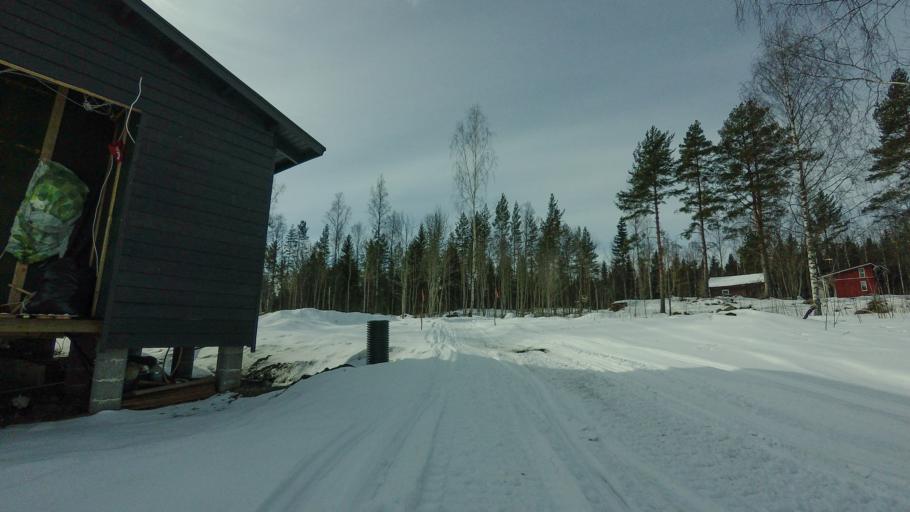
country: FI
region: Southern Savonia
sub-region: Savonlinna
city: Rantasalmi
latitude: 62.1206
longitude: 28.6027
